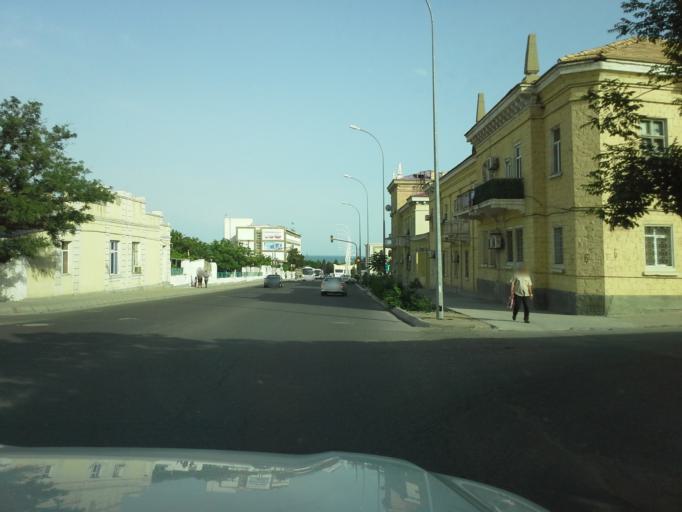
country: TM
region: Balkan
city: Turkmenbasy
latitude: 40.0069
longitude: 52.9927
